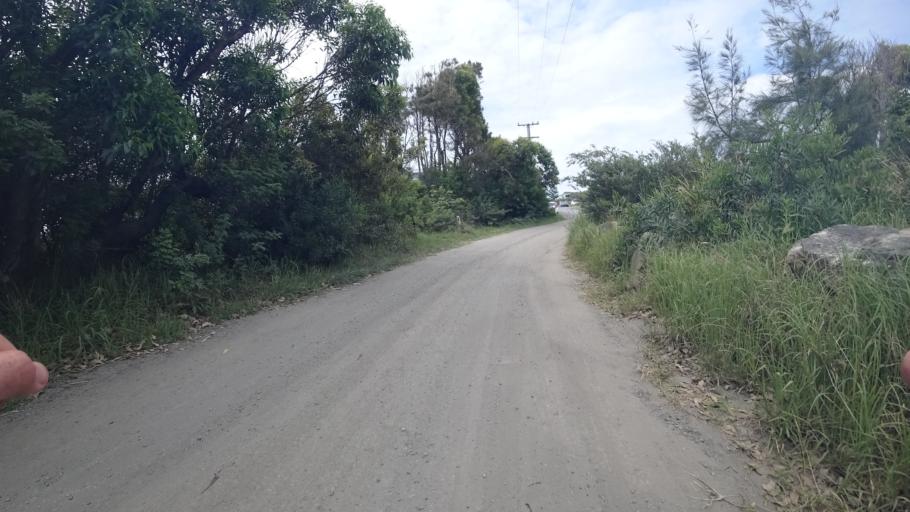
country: AU
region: New South Wales
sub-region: Shoalhaven Shire
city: Milton
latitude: -35.2555
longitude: 150.5259
